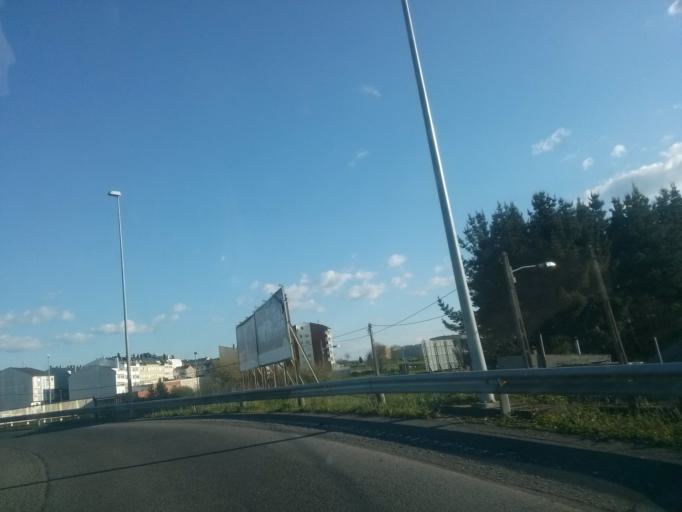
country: ES
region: Galicia
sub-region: Provincia de Lugo
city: Lugo
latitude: 43.0289
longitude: -7.5746
